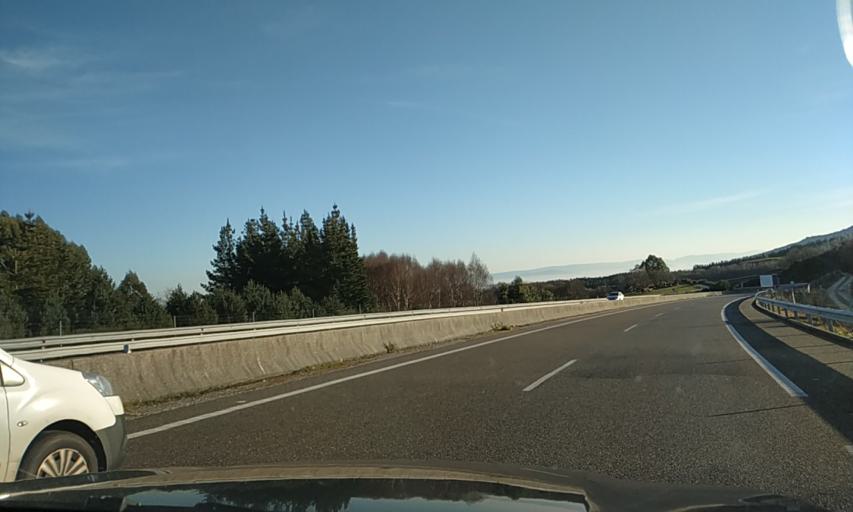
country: ES
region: Galicia
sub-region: Provincia de Pontevedra
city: Dozon
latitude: 42.5491
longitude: -8.0184
